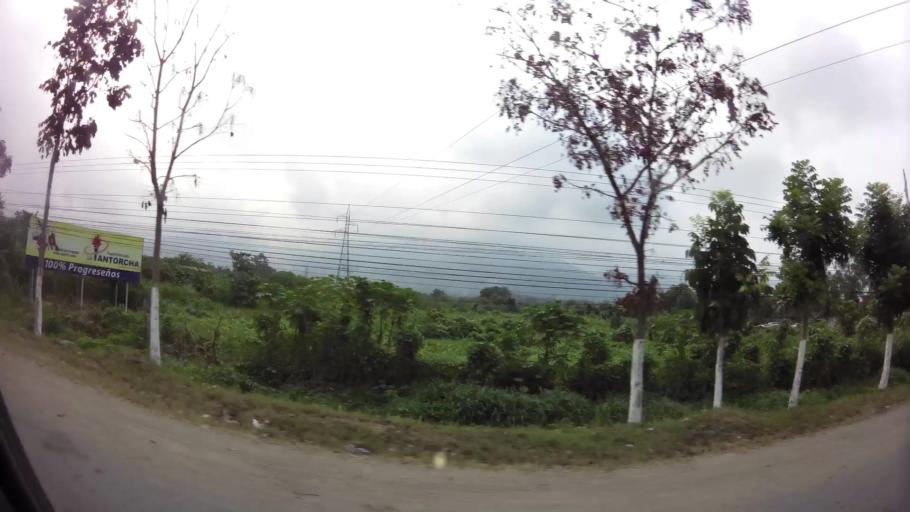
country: HN
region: Yoro
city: El Progreso
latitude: 15.4130
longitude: -87.8032
